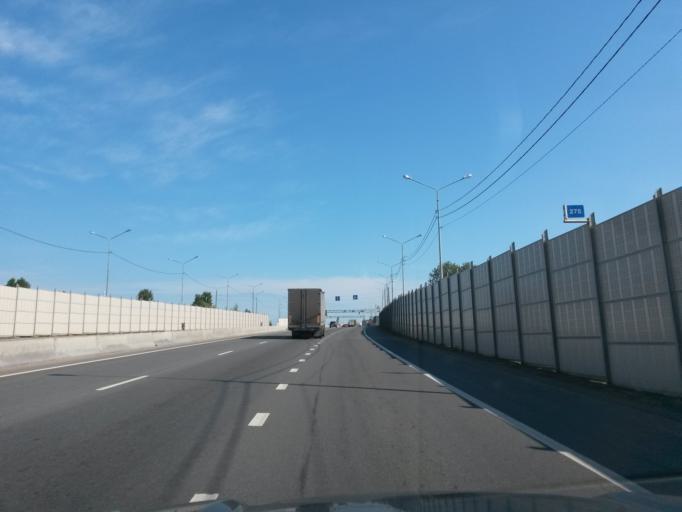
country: RU
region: Jaroslavl
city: Yaroslavl
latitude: 57.7047
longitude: 39.9006
